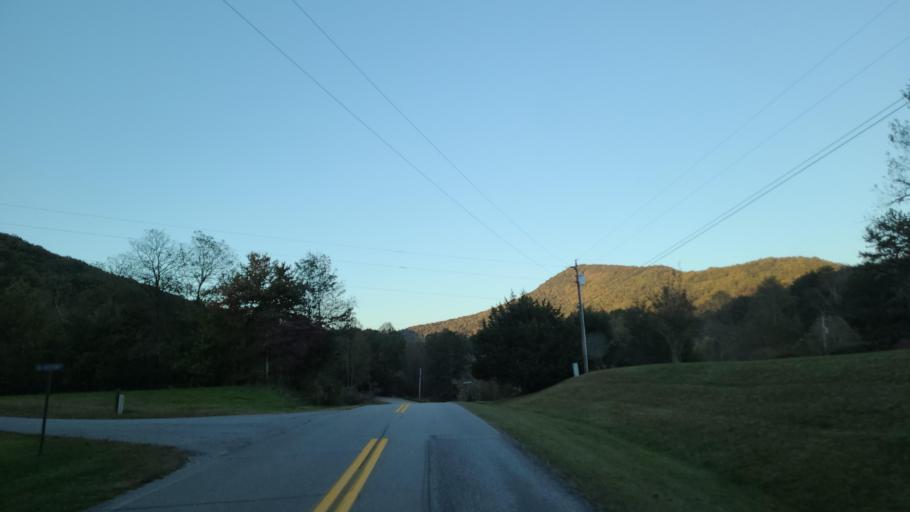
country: US
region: Georgia
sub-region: Union County
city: Blairsville
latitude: 34.8632
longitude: -83.8888
